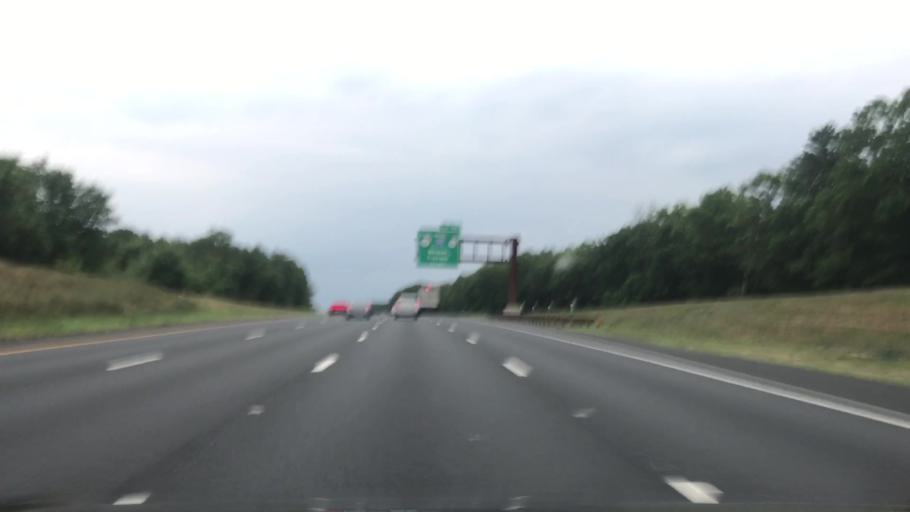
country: US
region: New Jersey
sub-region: Monmouth County
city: Ramtown
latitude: 40.1529
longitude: -74.1045
